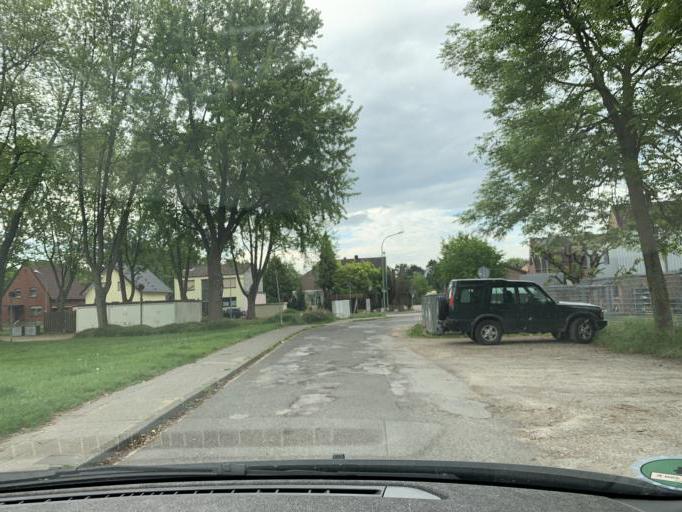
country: DE
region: North Rhine-Westphalia
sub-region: Regierungsbezirk Koln
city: Dueren
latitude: 50.8294
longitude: 6.4649
